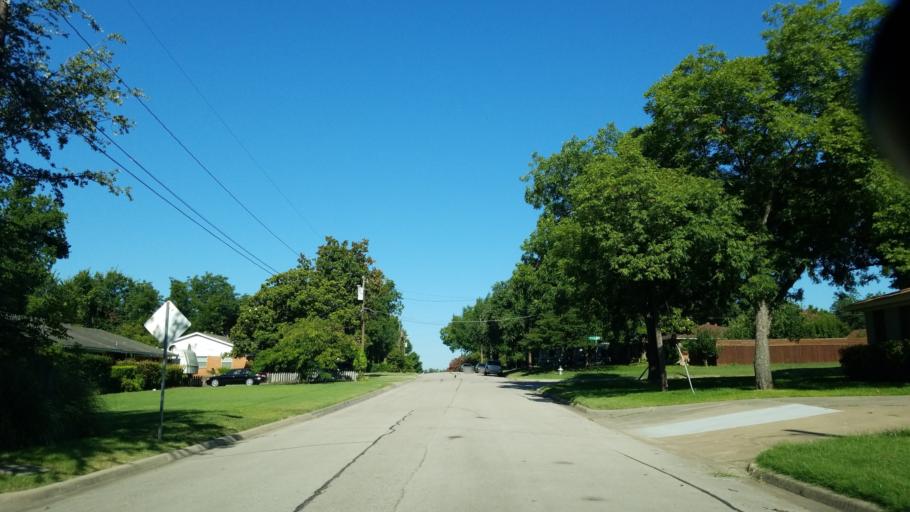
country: US
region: Texas
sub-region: Dallas County
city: Carrollton
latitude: 32.9507
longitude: -96.8996
